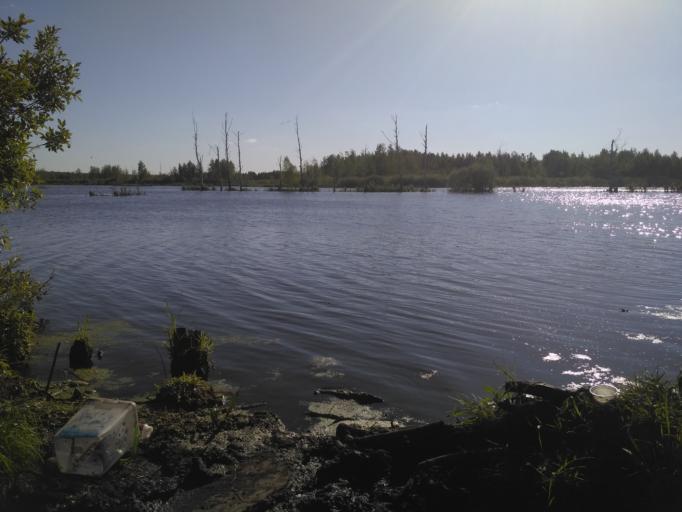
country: RU
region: Moskovskaya
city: Vereya
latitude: 55.7644
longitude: 39.1143
